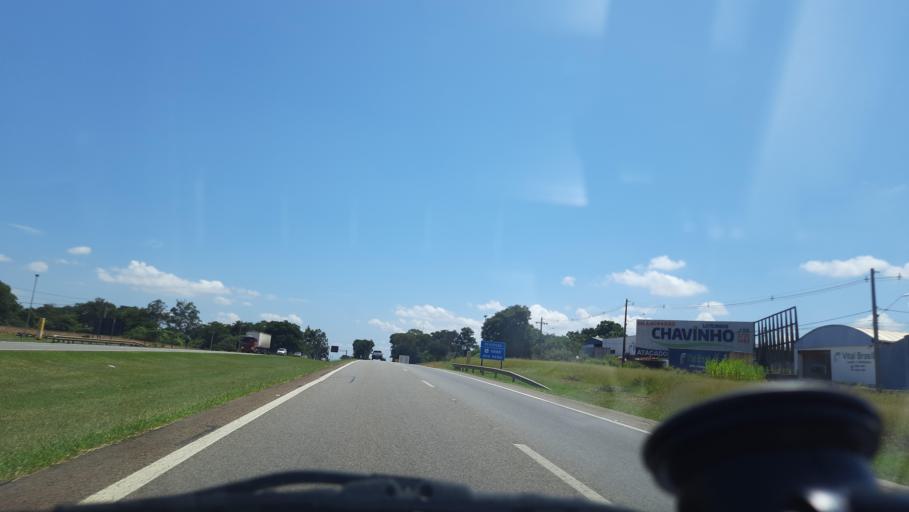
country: BR
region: Sao Paulo
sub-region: Mogi-Mirim
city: Mogi Mirim
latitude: -22.4670
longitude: -46.9819
